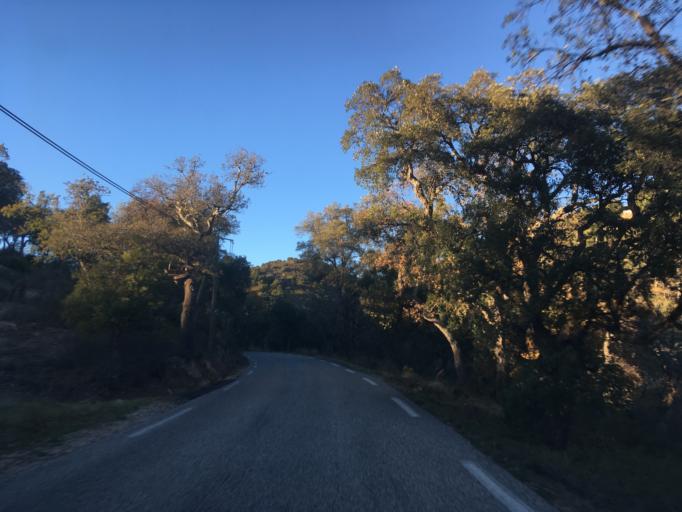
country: FR
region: Provence-Alpes-Cote d'Azur
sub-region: Departement du Var
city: Le Plan-de-la-Tour
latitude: 43.2947
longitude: 6.5594
